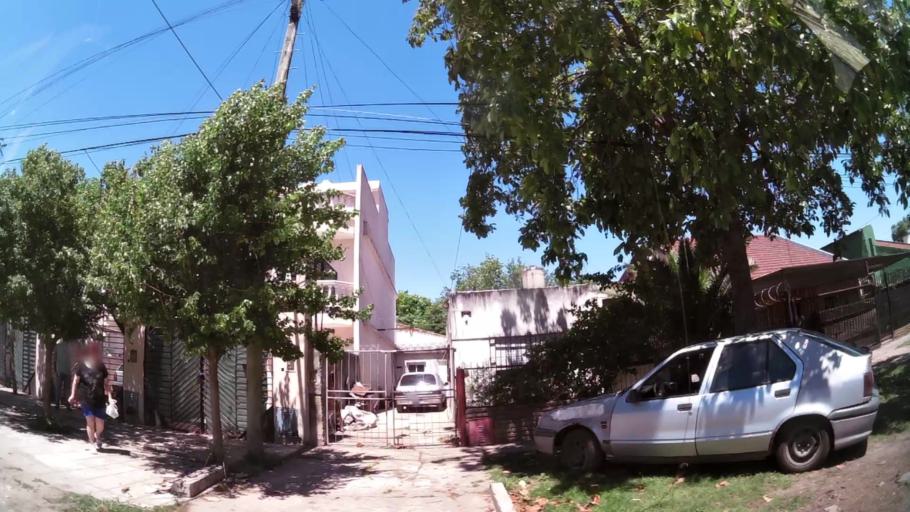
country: AR
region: Buenos Aires
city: Hurlingham
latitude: -34.5042
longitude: -58.6784
